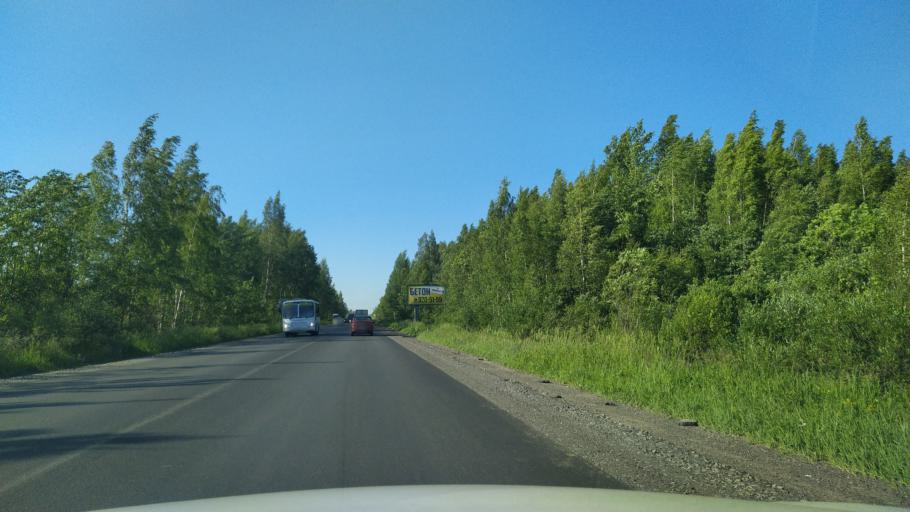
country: RU
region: Leningrad
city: Novoye Devyatkino
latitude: 60.0733
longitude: 30.4962
